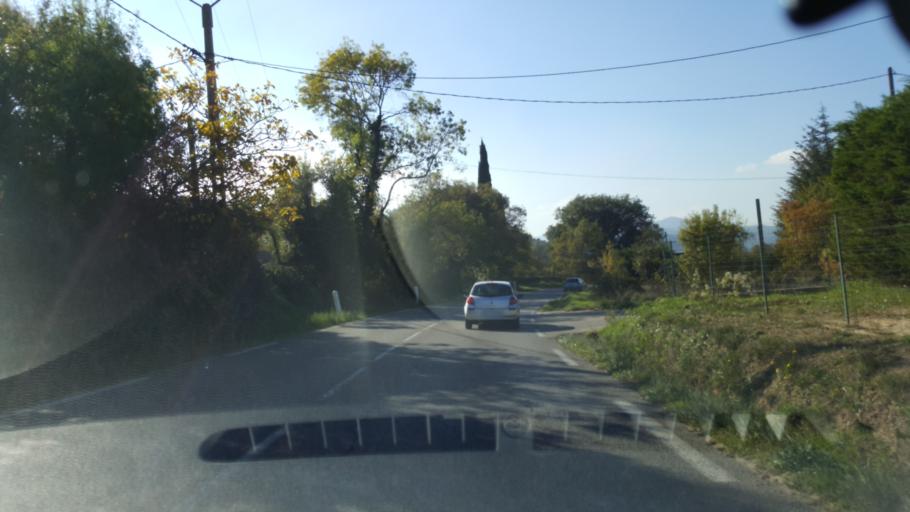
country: FR
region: Provence-Alpes-Cote d'Azur
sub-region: Departement des Bouches-du-Rhone
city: Auriol
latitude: 43.3708
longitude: 5.6644
